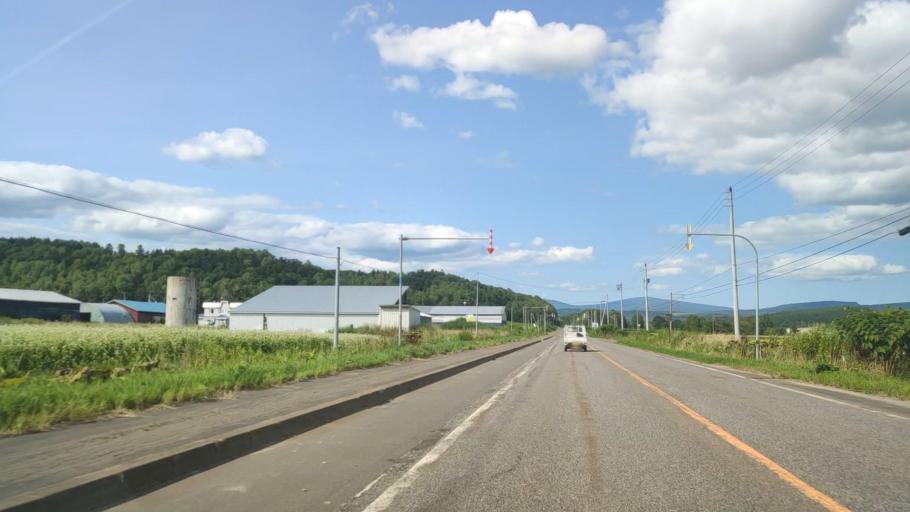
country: JP
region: Hokkaido
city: Nayoro
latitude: 44.4002
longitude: 142.3959
